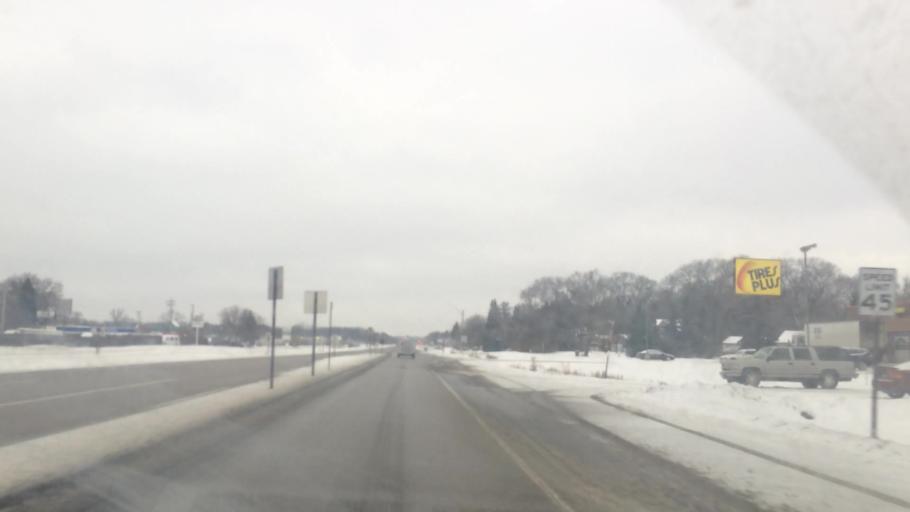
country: US
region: Minnesota
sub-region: Anoka County
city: Lexington
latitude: 45.1408
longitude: -93.1646
